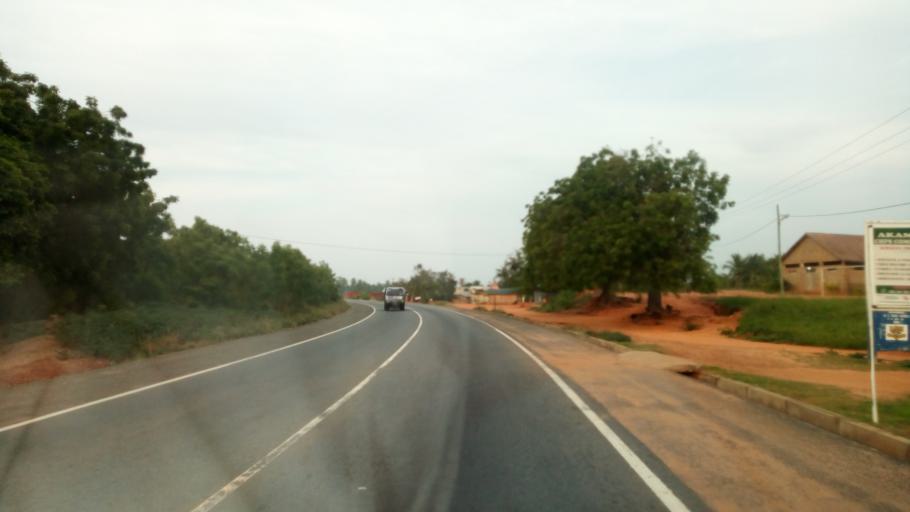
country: TG
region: Maritime
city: Lome
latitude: 6.1044
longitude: 1.1030
